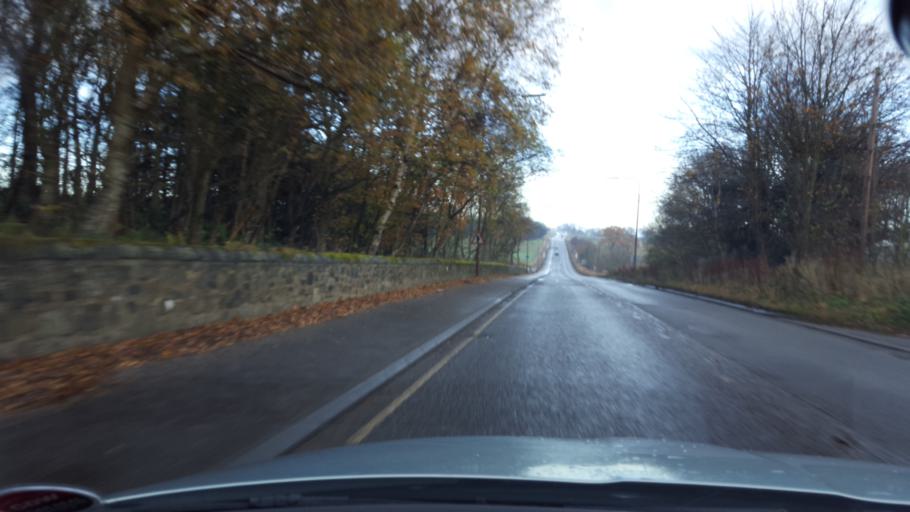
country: GB
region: Scotland
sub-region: Edinburgh
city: Queensferry
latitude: 55.9722
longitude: -3.3999
